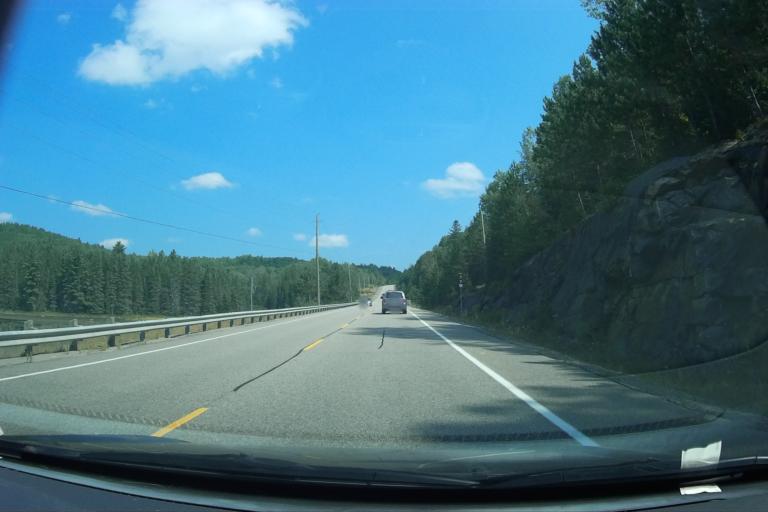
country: CA
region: Ontario
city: Bancroft
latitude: 45.5761
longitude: -78.4169
